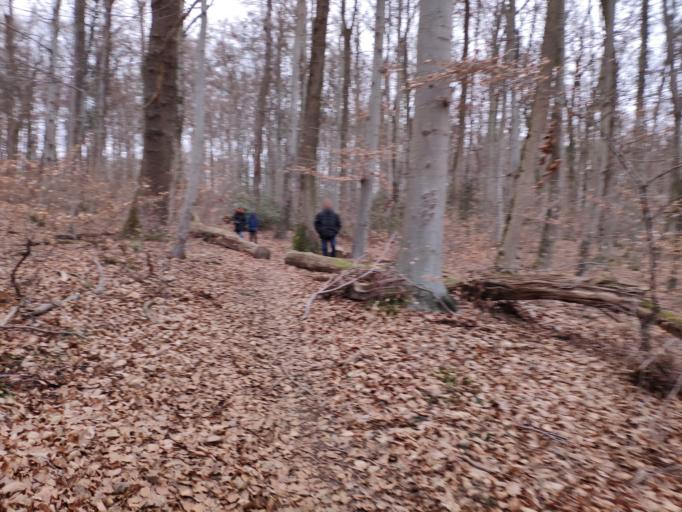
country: DE
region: Baden-Wuerttemberg
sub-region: Freiburg Region
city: Inzlingen
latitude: 47.5926
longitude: 7.6792
